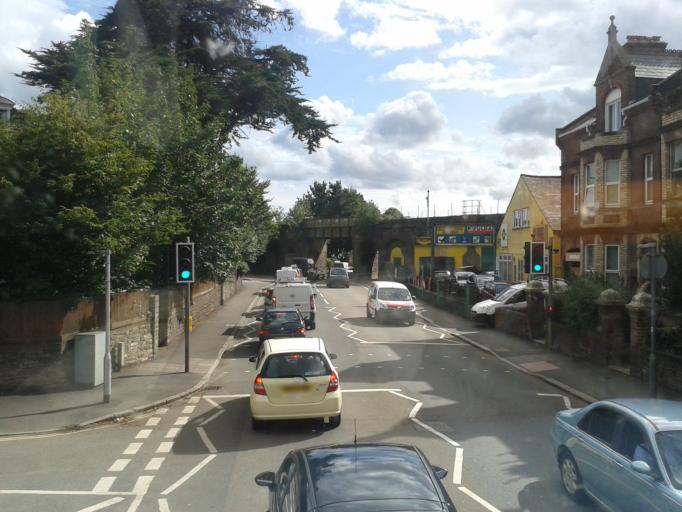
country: GB
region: England
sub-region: Devon
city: Exeter
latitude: 50.7156
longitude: -3.5359
